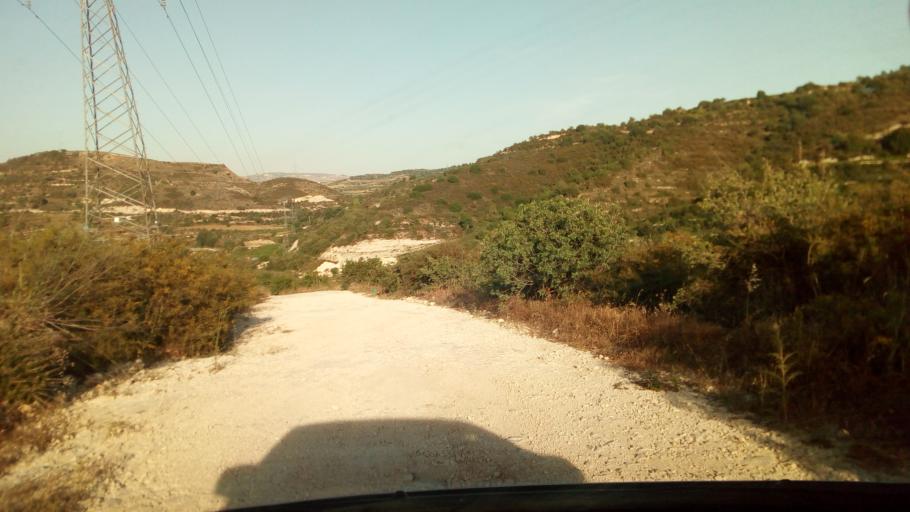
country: CY
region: Pafos
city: Tala
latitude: 34.8717
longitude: 32.4677
